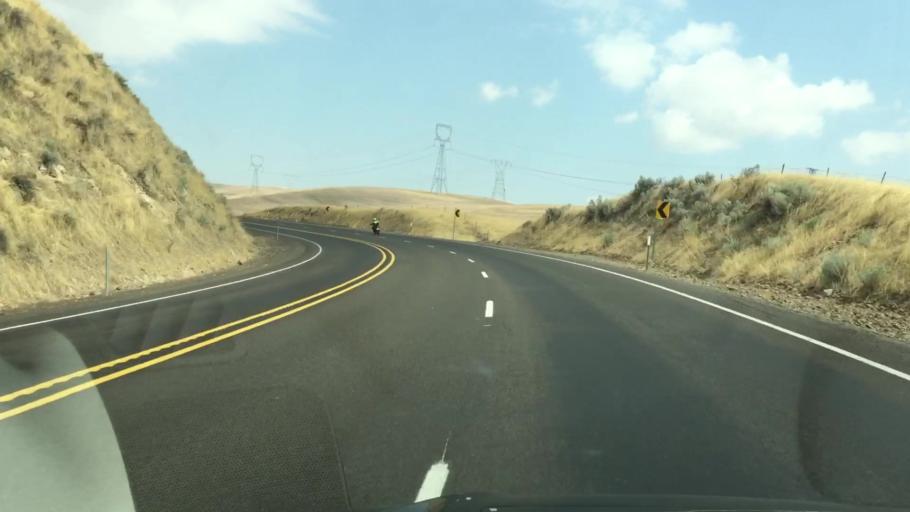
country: US
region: Oregon
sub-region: Wasco County
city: The Dalles
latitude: 45.5646
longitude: -121.1023
